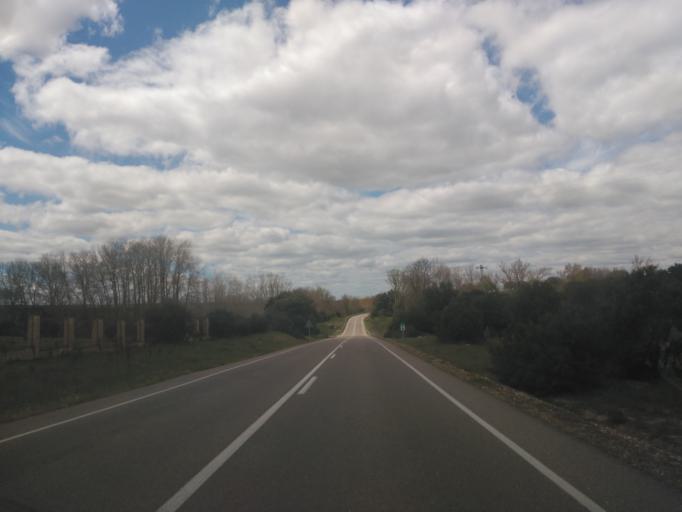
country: ES
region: Castille and Leon
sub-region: Provincia de Salamanca
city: Florida de Liebana
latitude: 41.0390
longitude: -5.7465
